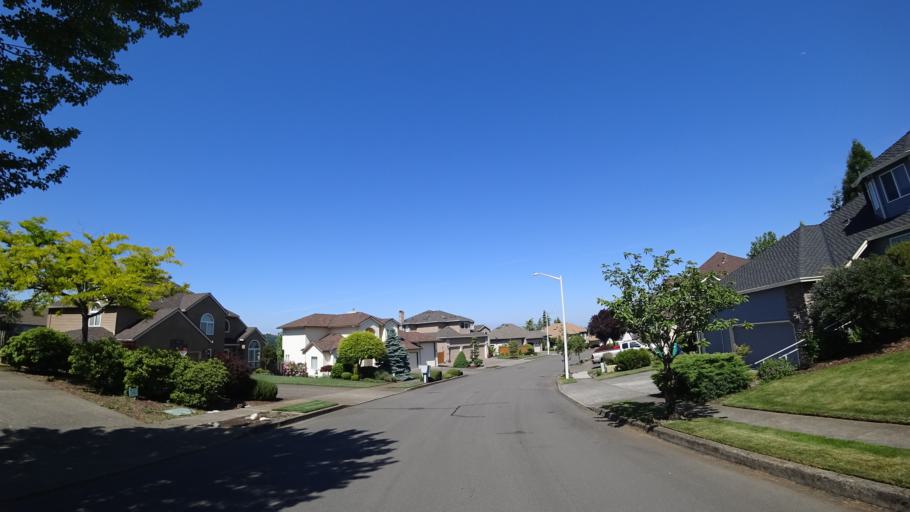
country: US
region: Oregon
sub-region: Multnomah County
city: Gresham
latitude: 45.4804
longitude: -122.4737
